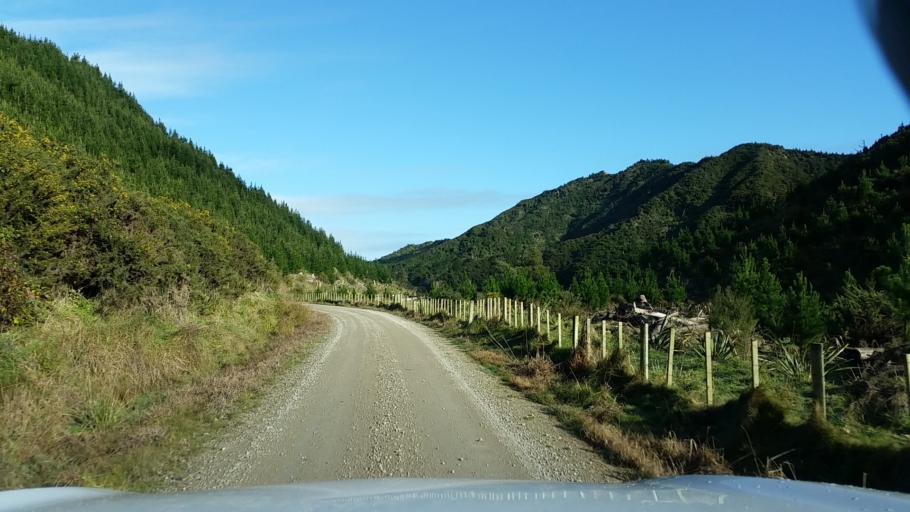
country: NZ
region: Taranaki
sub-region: South Taranaki District
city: Patea
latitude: -39.6921
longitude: 174.7522
